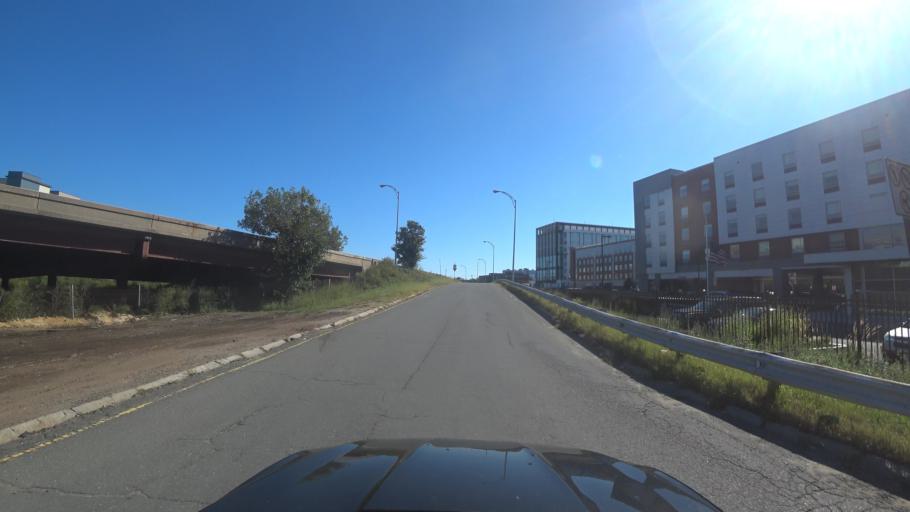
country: US
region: Massachusetts
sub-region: Suffolk County
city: Chelsea
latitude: 42.3998
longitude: -71.0389
